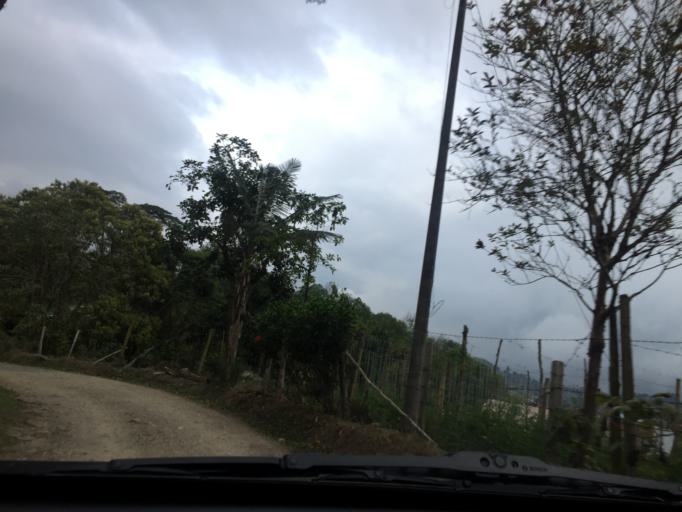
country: CO
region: Cundinamarca
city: San Antonio del Tequendama
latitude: 4.6772
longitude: -74.3758
